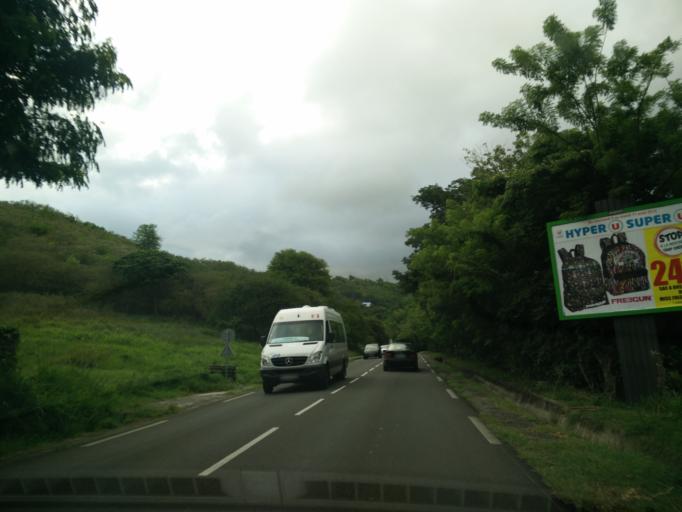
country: MQ
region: Martinique
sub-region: Martinique
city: Le Marin
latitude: 14.4719
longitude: -60.8581
